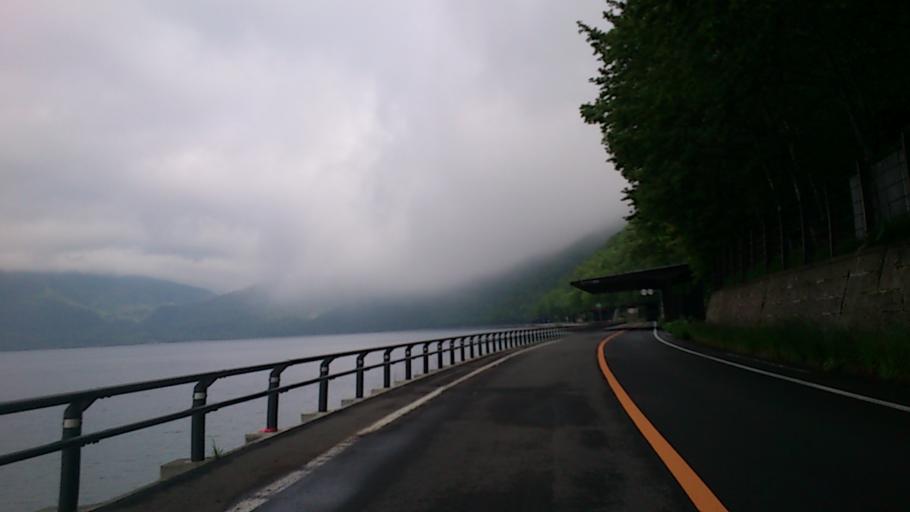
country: JP
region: Hokkaido
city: Shiraoi
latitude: 42.7894
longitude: 141.3744
